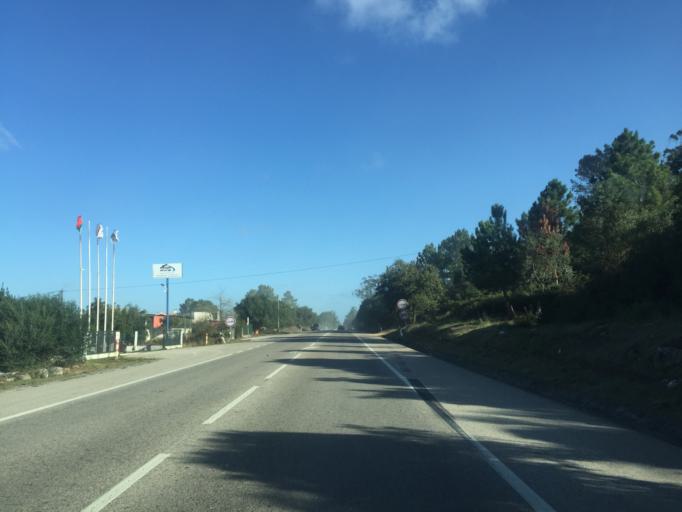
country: PT
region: Leiria
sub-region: Alcobaca
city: Turquel
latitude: 39.4535
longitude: -8.9484
